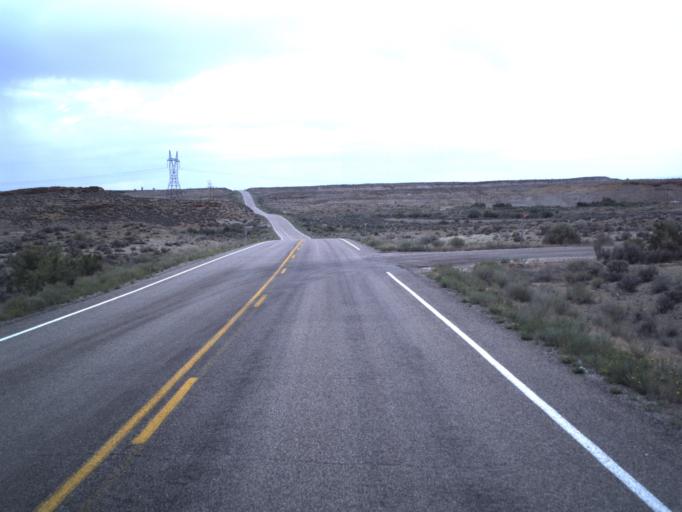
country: US
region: Colorado
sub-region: Rio Blanco County
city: Rangely
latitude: 40.0671
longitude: -109.2004
